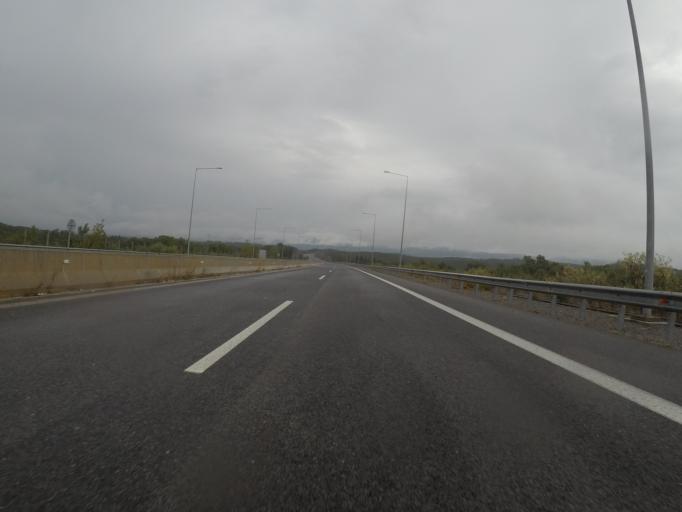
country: GR
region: Peloponnese
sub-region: Nomos Arkadias
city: Megalopoli
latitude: 37.3464
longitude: 22.1120
